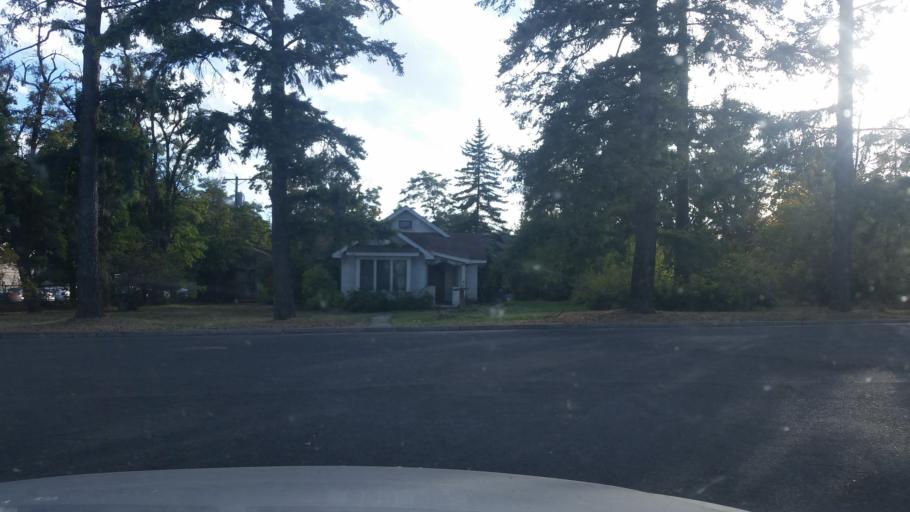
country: US
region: Washington
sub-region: Spokane County
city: Cheney
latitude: 47.4852
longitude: -117.5809
